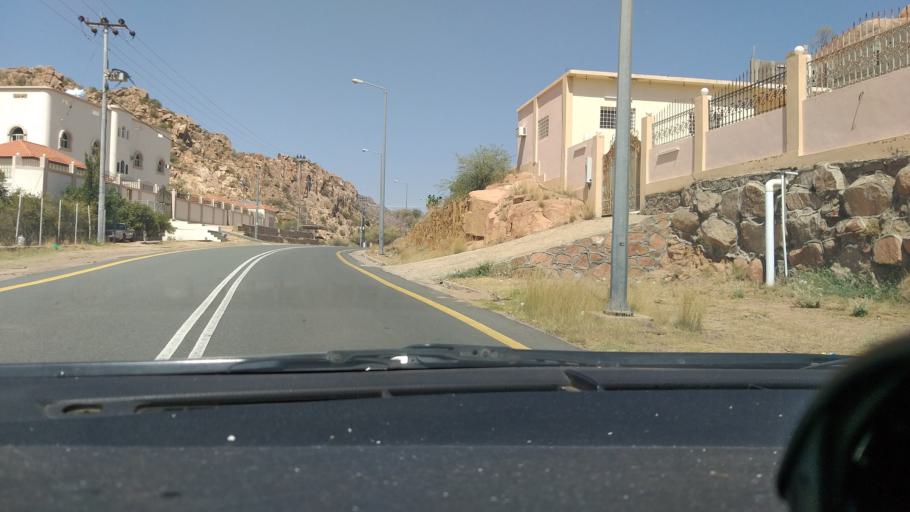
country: SA
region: Makkah
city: Ash Shafa
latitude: 21.0921
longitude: 40.3707
